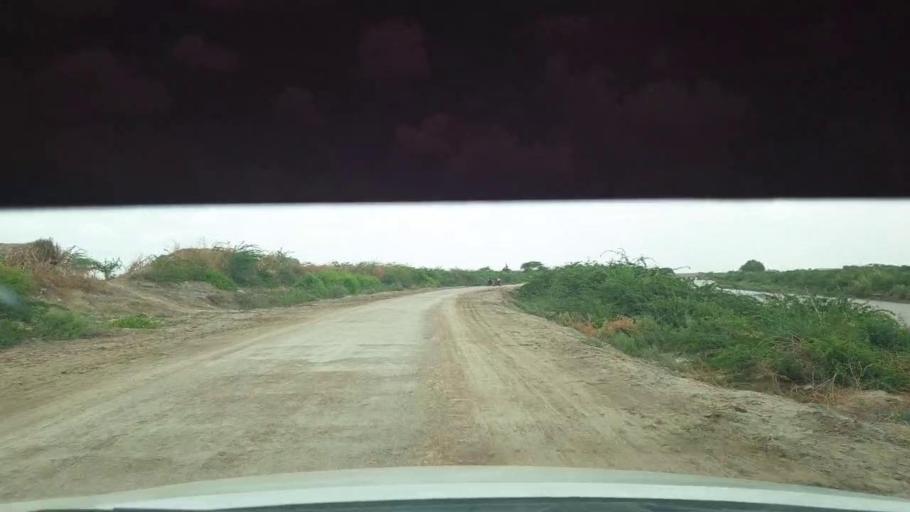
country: PK
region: Sindh
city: Kadhan
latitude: 24.4702
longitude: 69.0518
